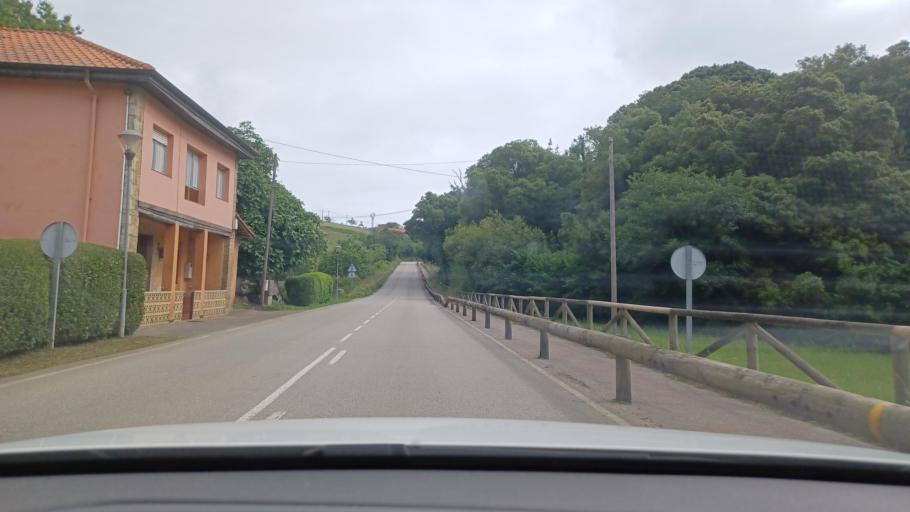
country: ES
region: Asturias
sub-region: Province of Asturias
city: Ribadesella
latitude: 43.4581
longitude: -5.0936
